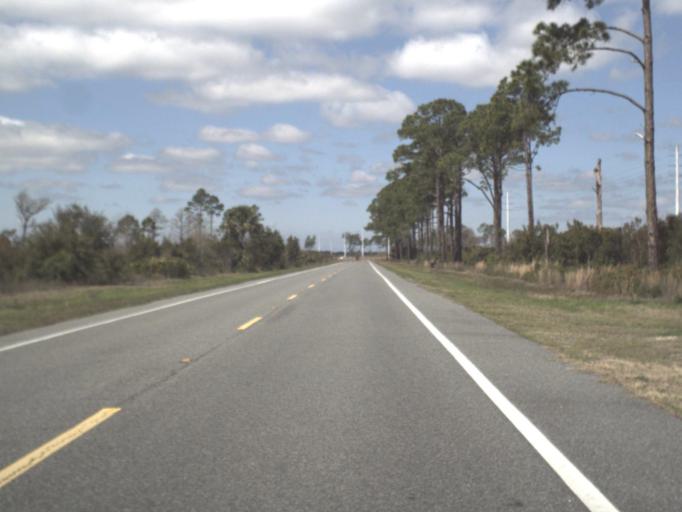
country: US
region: Florida
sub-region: Franklin County
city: Apalachicola
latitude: 29.7226
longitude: -85.0733
